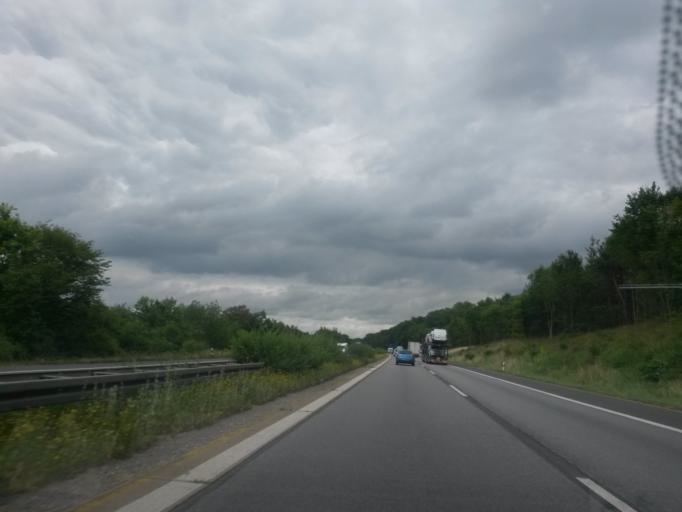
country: DE
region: Bavaria
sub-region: Regierungsbezirk Unterfranken
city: Albertshofen
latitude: 49.7852
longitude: 10.1952
